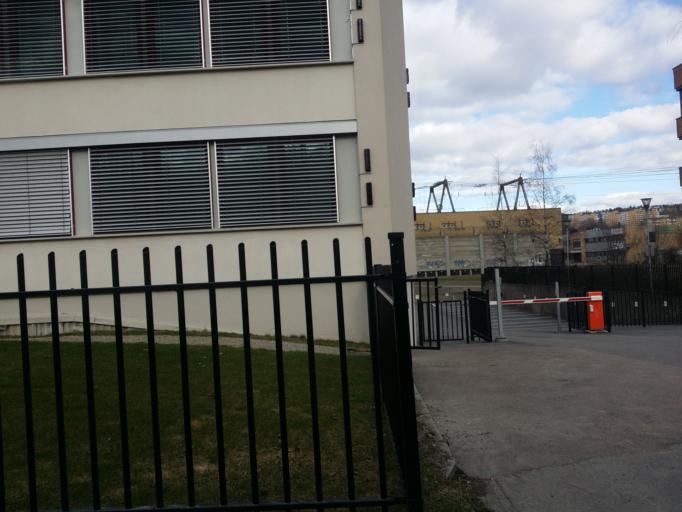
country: NO
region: Oslo
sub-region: Oslo
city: Oslo
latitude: 59.9120
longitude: 10.8162
